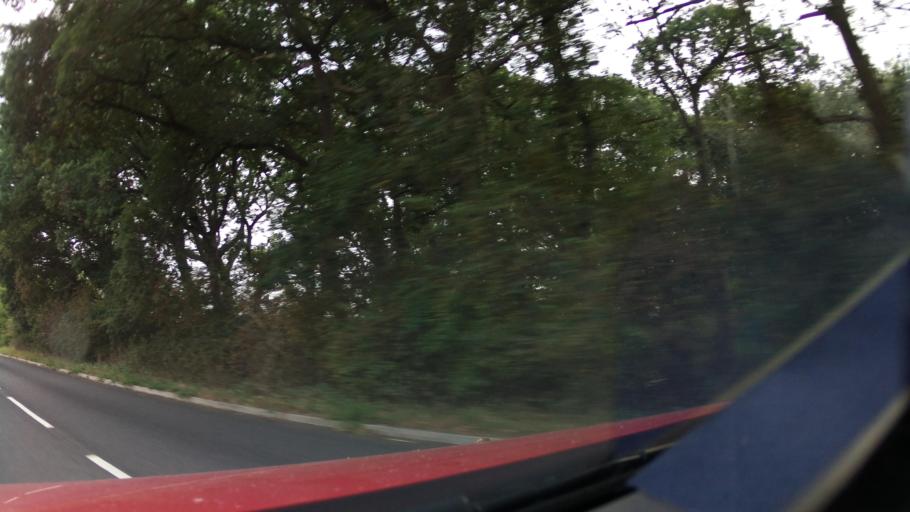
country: GB
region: England
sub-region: Nottinghamshire
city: South Collingham
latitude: 53.1467
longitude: -0.6691
